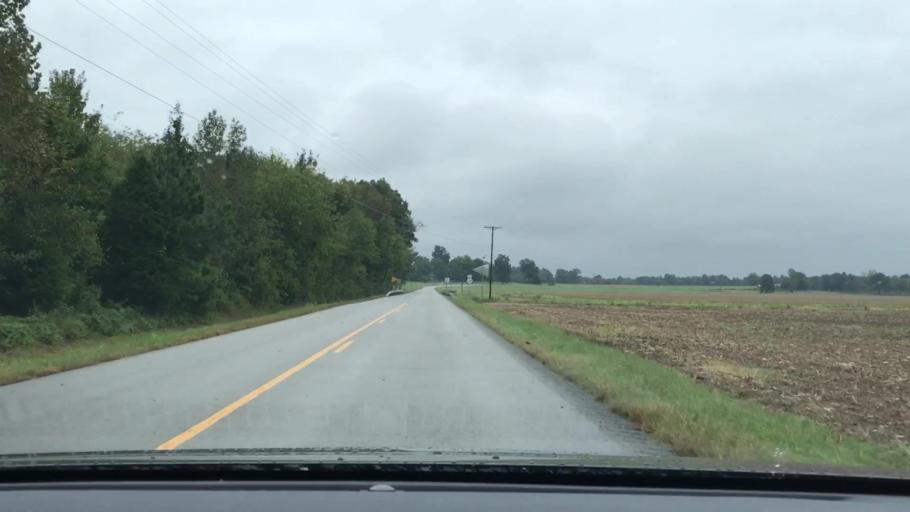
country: US
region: Kentucky
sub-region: McLean County
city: Calhoun
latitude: 37.4727
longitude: -87.2390
